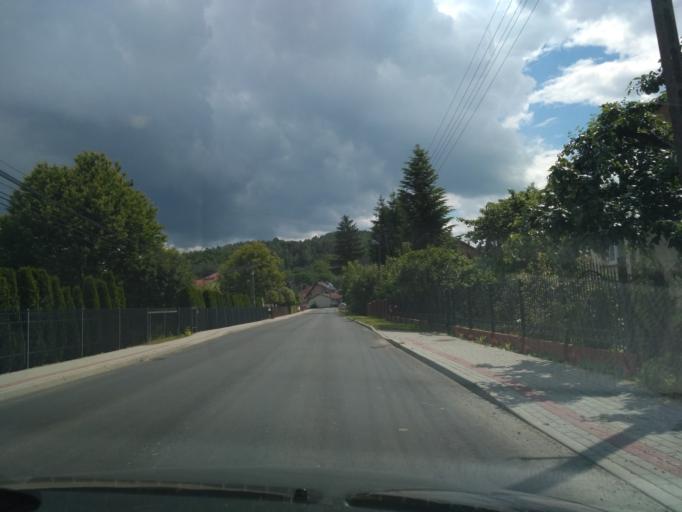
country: PL
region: Subcarpathian Voivodeship
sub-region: Powiat rzeszowski
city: Blazowa
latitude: 49.8802
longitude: 22.0919
